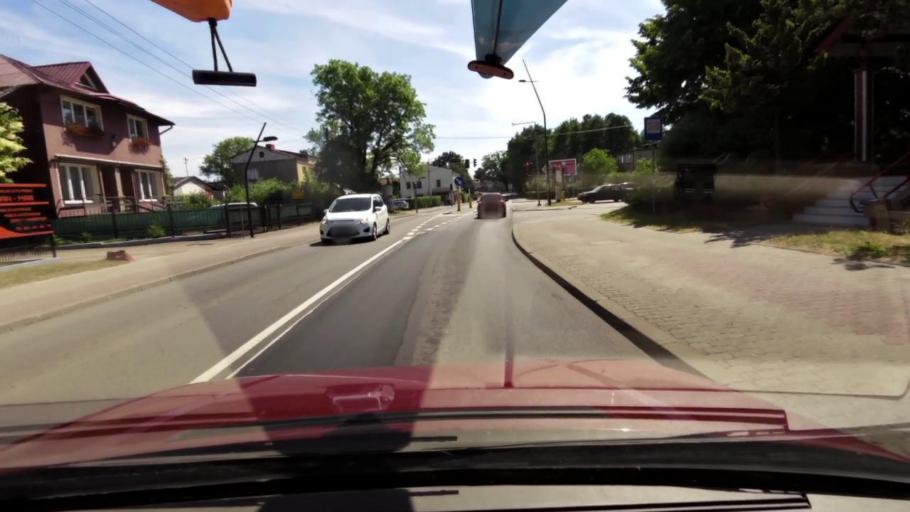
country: PL
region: Pomeranian Voivodeship
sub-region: Powiat slupski
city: Kobylnica
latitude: 54.4410
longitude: 16.9988
